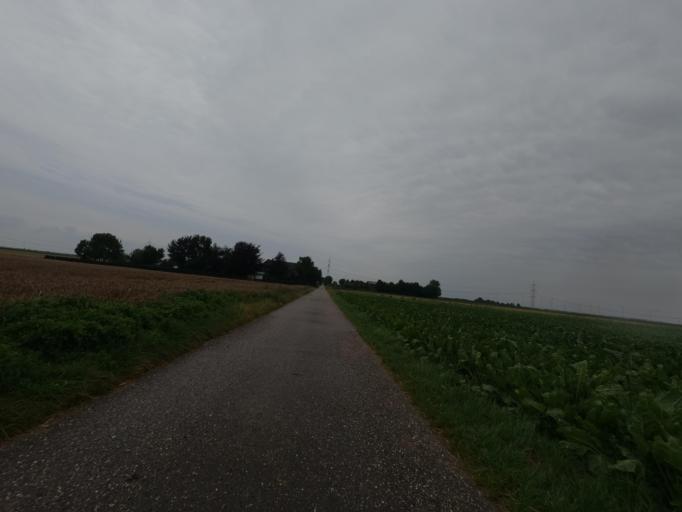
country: DE
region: North Rhine-Westphalia
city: Geilenkirchen
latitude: 50.9563
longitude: 6.1596
